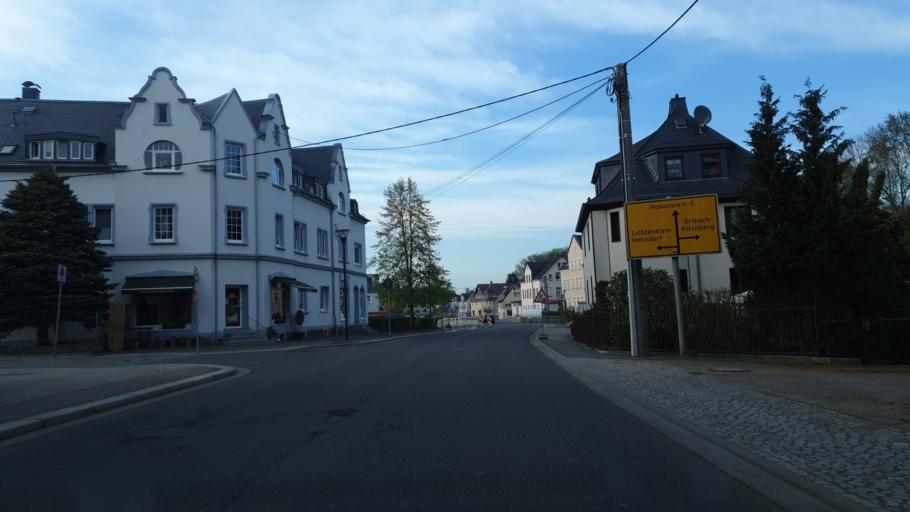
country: DE
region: Saxony
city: Gersdorf
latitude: 50.7565
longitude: 12.7078
